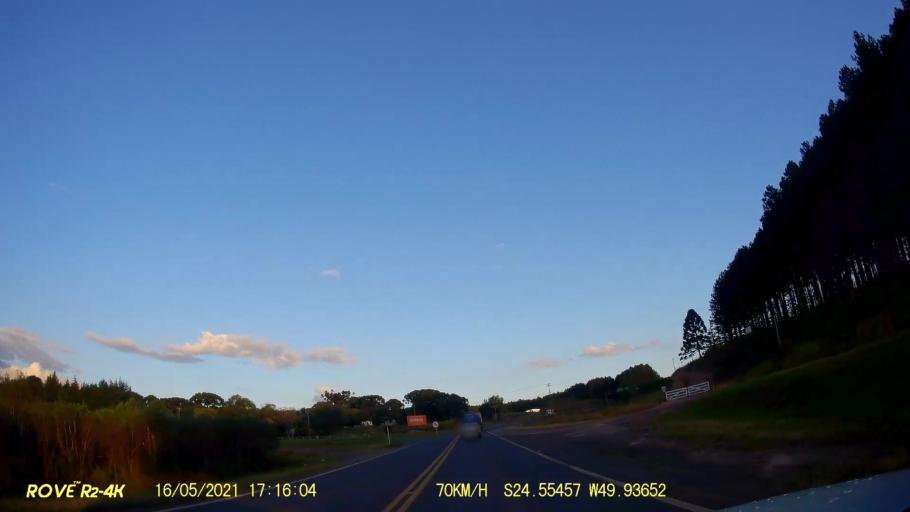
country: BR
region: Parana
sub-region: Pirai Do Sul
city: Pirai do Sul
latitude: -24.5547
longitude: -49.9363
